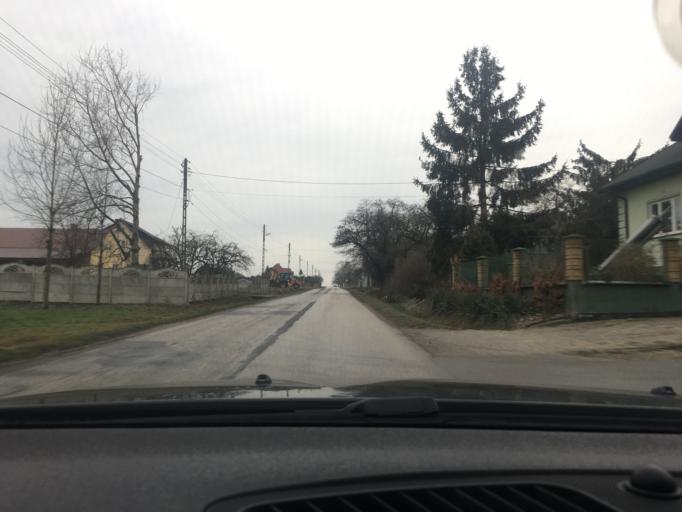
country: PL
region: Swietokrzyskie
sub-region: Powiat jedrzejowski
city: Jedrzejow
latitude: 50.6409
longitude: 20.3527
